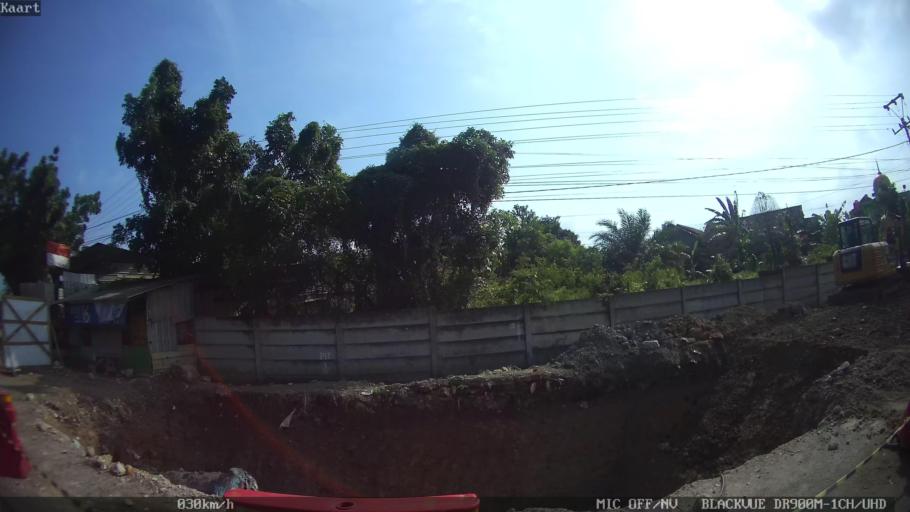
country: ID
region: Lampung
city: Kedaton
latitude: -5.3621
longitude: 105.2580
